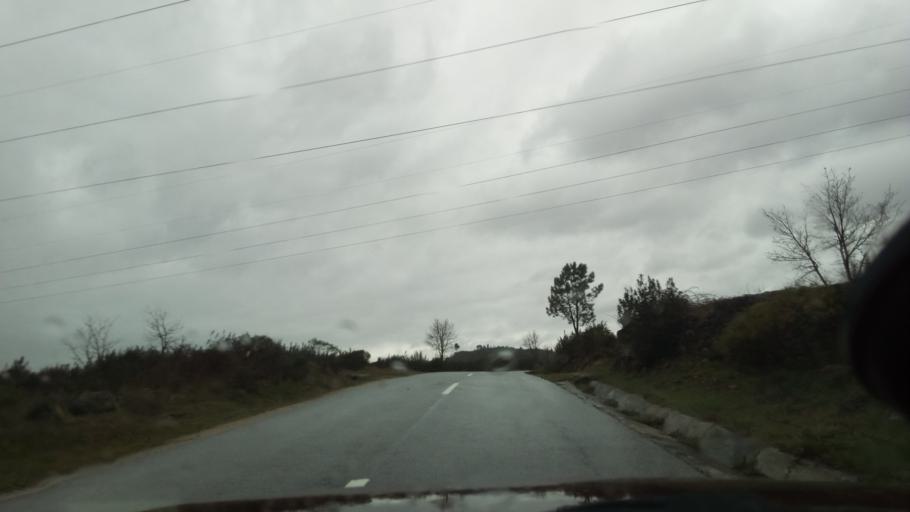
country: PT
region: Guarda
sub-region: Fornos de Algodres
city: Fornos de Algodres
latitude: 40.5763
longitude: -7.5094
